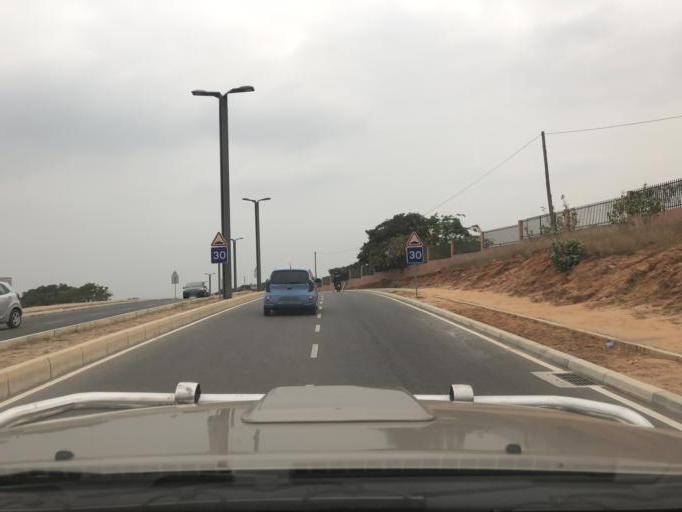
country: AO
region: Luanda
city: Luanda
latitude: -8.8974
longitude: 13.1753
